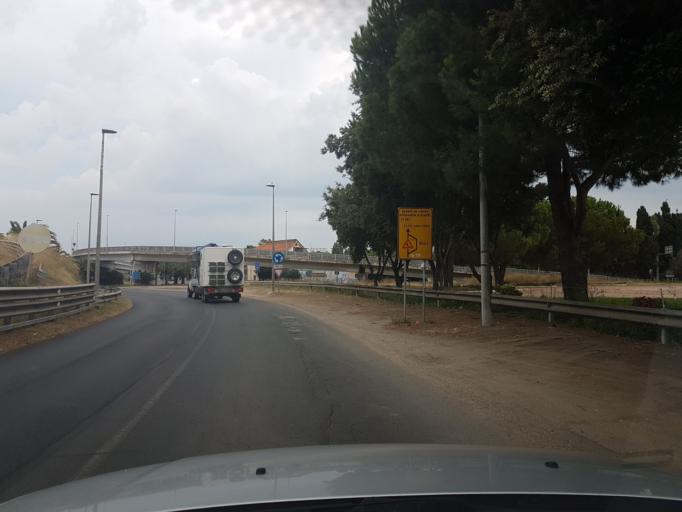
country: IT
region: Sardinia
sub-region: Provincia di Oristano
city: Donigala Fenugheddu
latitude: 39.9276
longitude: 8.5770
